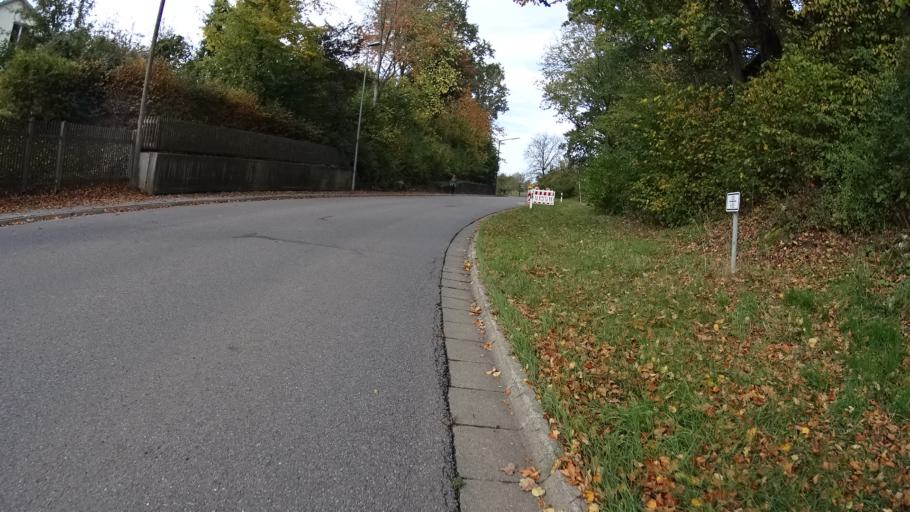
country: DE
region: Bavaria
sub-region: Upper Bavaria
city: Buxheim
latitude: 48.8266
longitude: 11.2753
